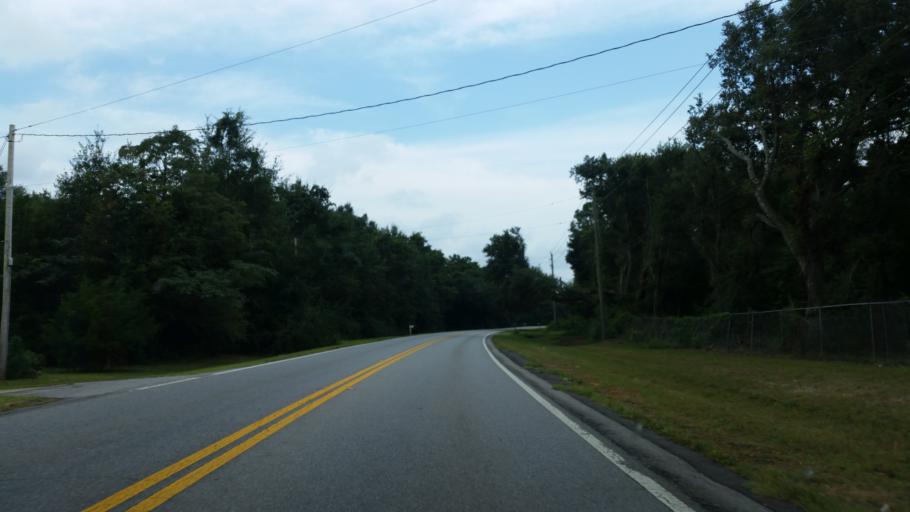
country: US
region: Florida
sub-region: Santa Rosa County
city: Pace
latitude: 30.6220
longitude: -87.1619
